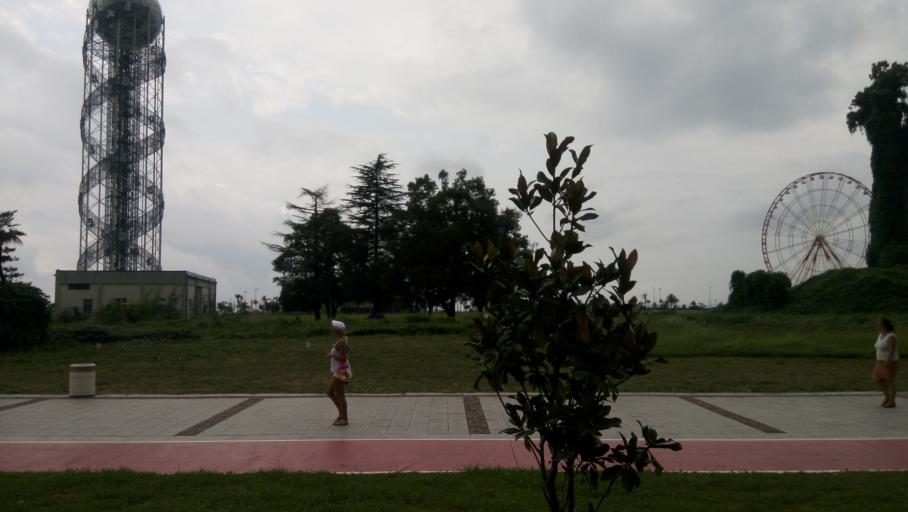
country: GE
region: Ajaria
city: Batumi
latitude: 41.6531
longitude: 41.6400
